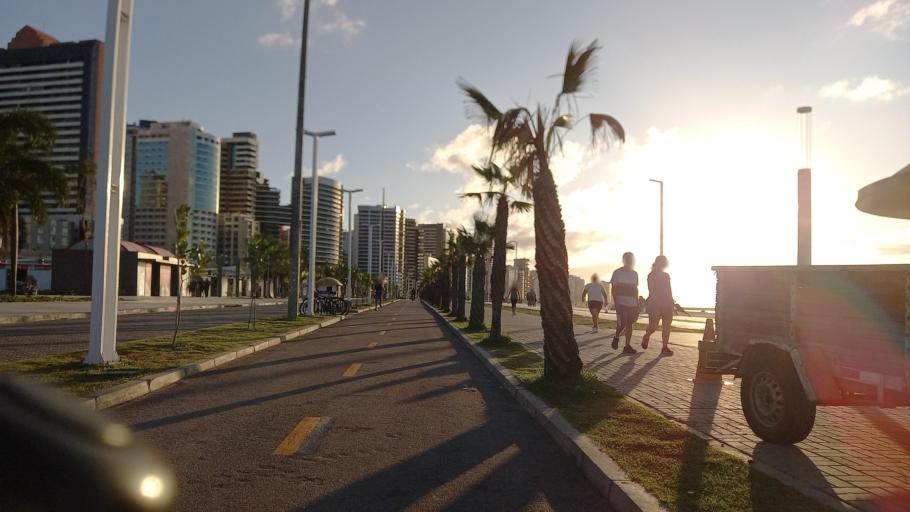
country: BR
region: Ceara
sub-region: Fortaleza
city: Fortaleza
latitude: -3.7249
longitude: -38.4949
